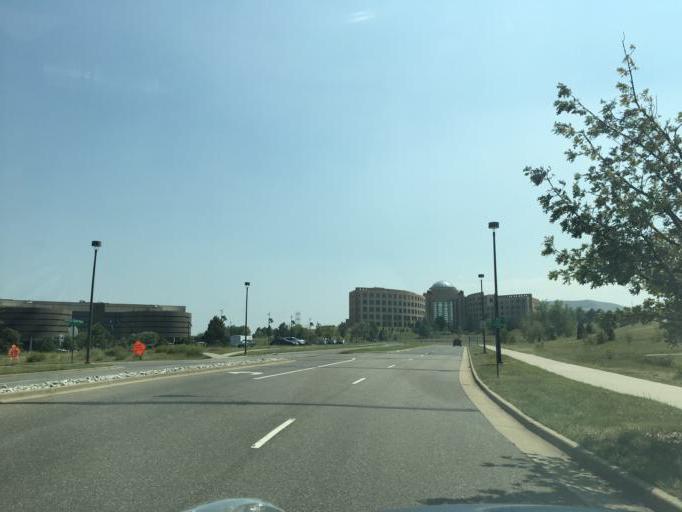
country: US
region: Colorado
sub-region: Jefferson County
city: West Pleasant View
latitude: 39.7311
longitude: -105.2060
